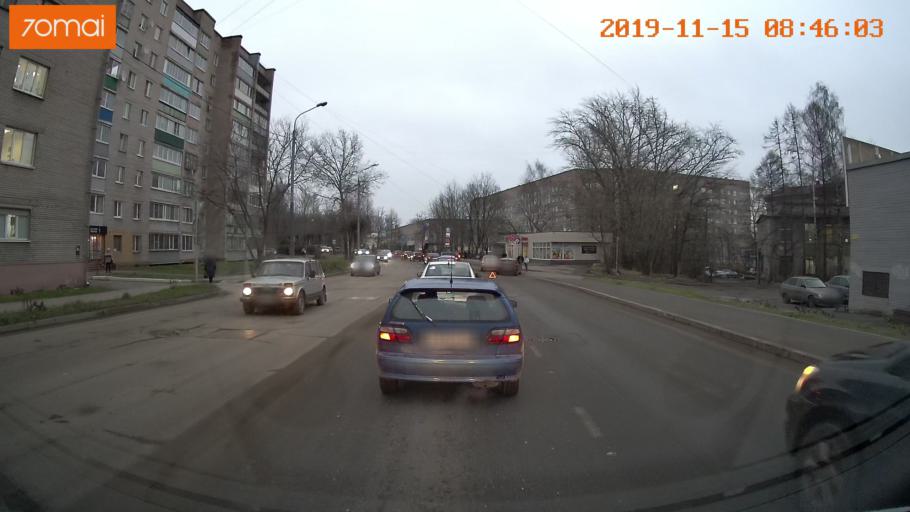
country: RU
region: Vologda
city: Cherepovets
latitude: 59.1188
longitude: 37.9053
